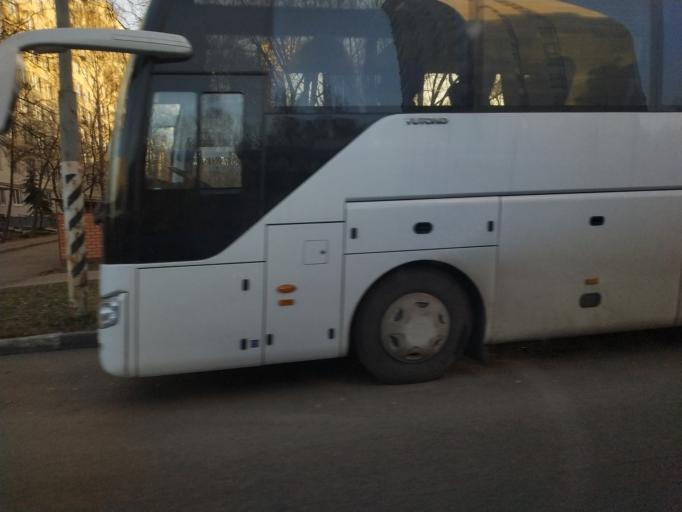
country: RU
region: Moscow
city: Chertanovo Yuzhnoye
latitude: 55.6023
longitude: 37.6107
